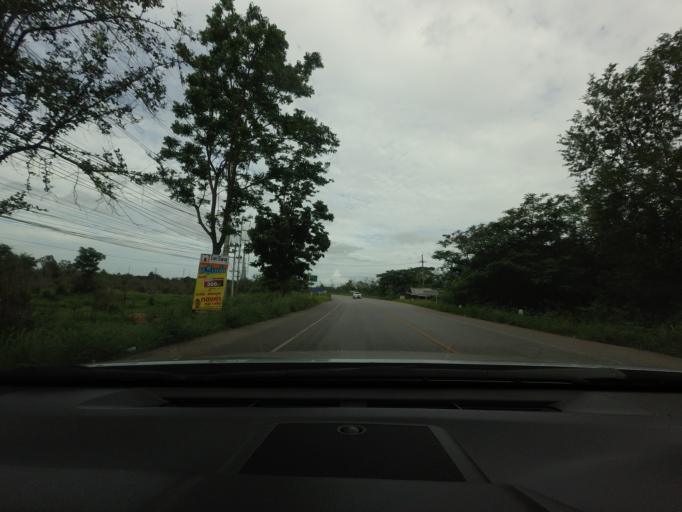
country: TH
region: Prachuap Khiri Khan
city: Hua Hin
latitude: 12.5770
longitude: 99.8631
